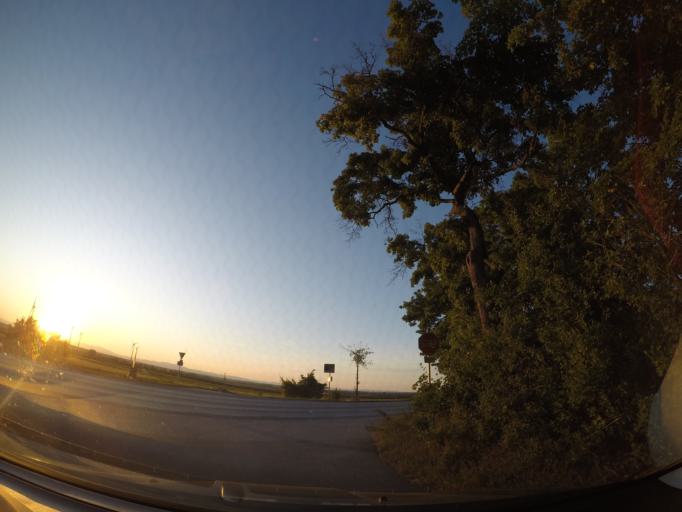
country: AT
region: Lower Austria
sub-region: Politischer Bezirk Bruck an der Leitha
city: Hof am Leithaberge
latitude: 47.9592
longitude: 16.5871
